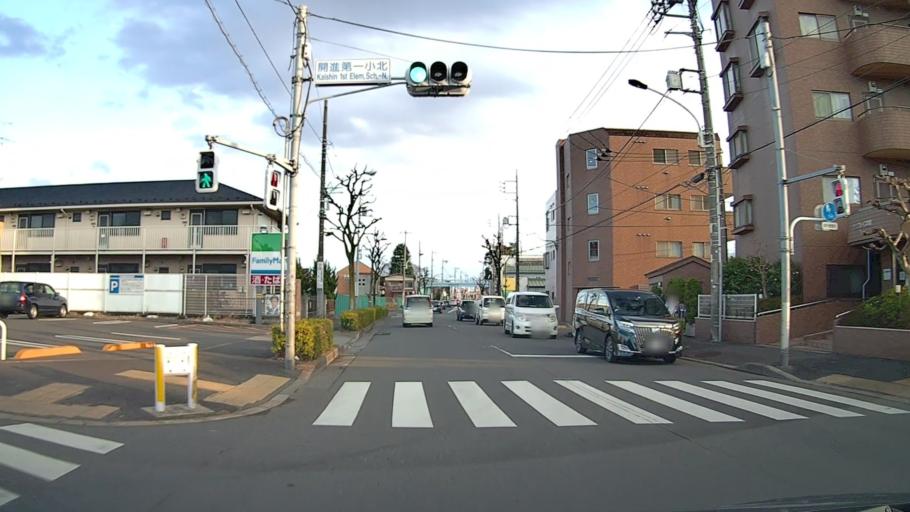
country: JP
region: Saitama
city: Wako
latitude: 35.7559
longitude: 139.6571
